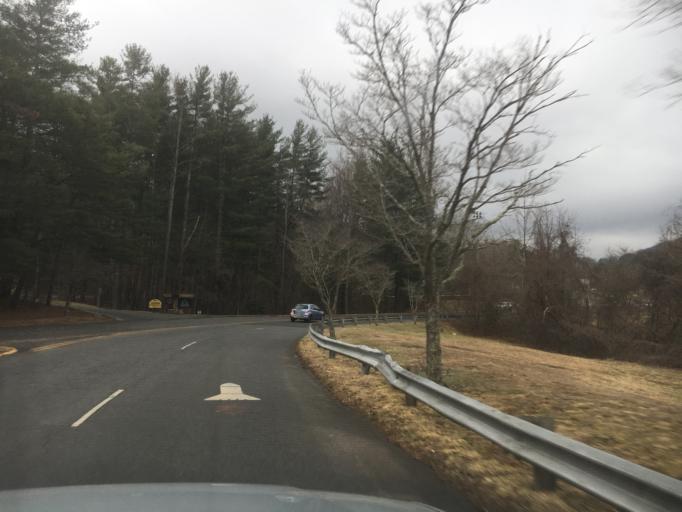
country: US
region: North Carolina
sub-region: Buncombe County
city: Biltmore Forest
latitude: 35.5499
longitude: -82.4755
